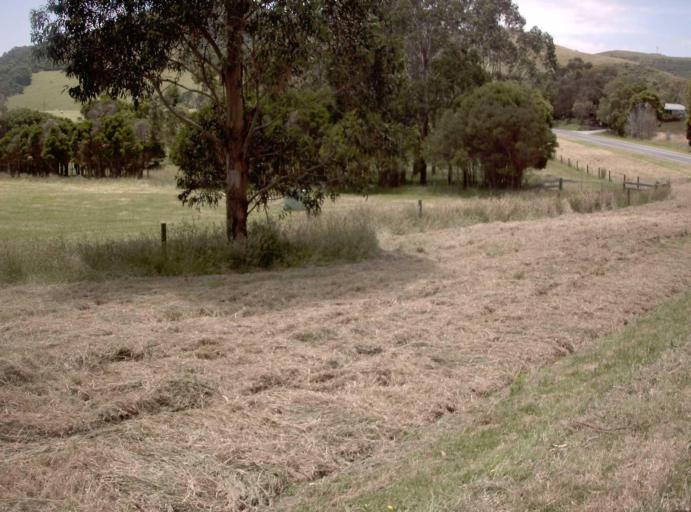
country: AU
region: Victoria
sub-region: Bass Coast
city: North Wonthaggi
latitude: -38.7180
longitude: 146.1070
